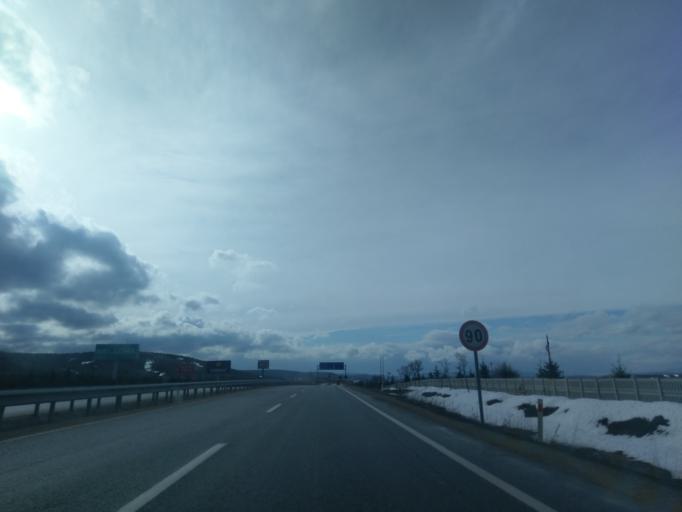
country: TR
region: Eskisehir
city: Inonu
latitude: 39.7099
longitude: 30.1664
